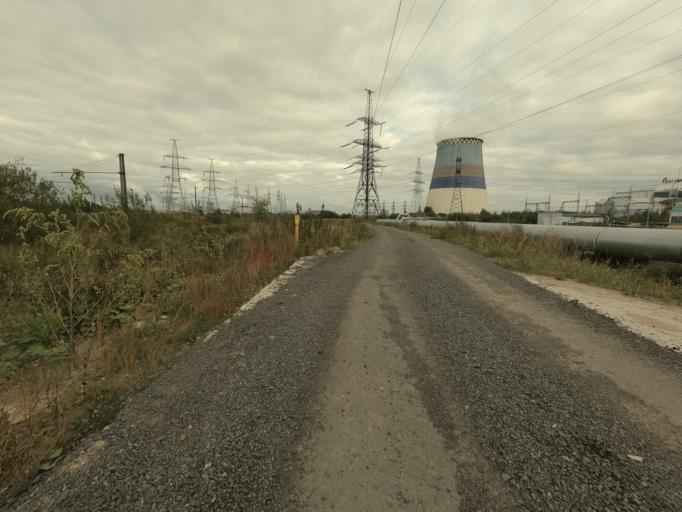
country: RU
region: St.-Petersburg
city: Obukhovo
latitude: 59.8302
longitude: 30.4473
